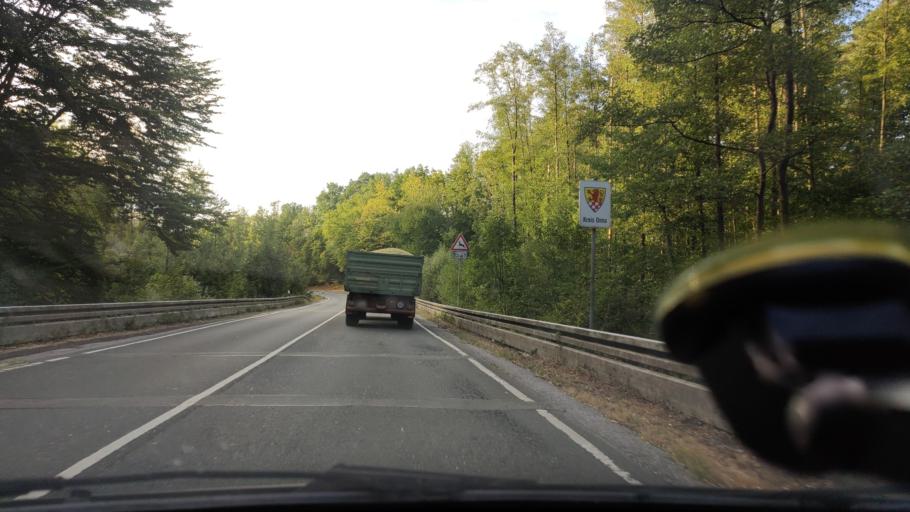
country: DE
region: North Rhine-Westphalia
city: Schwerte
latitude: 51.3905
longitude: 7.5856
